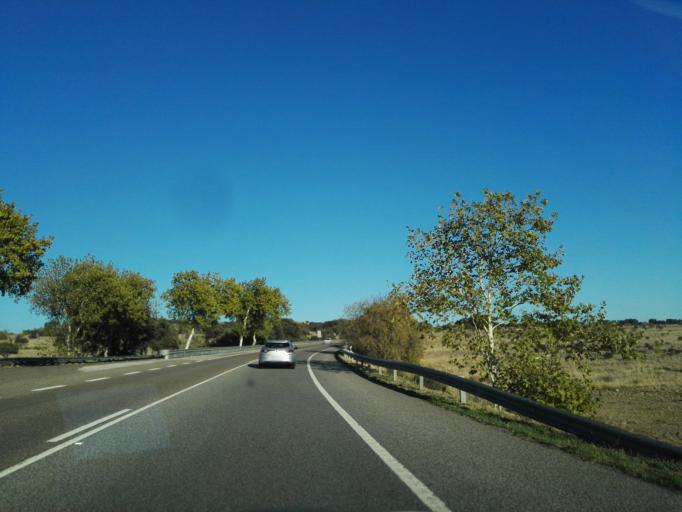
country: PT
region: Portalegre
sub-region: Elvas
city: Elvas
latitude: 38.8610
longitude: -7.3013
